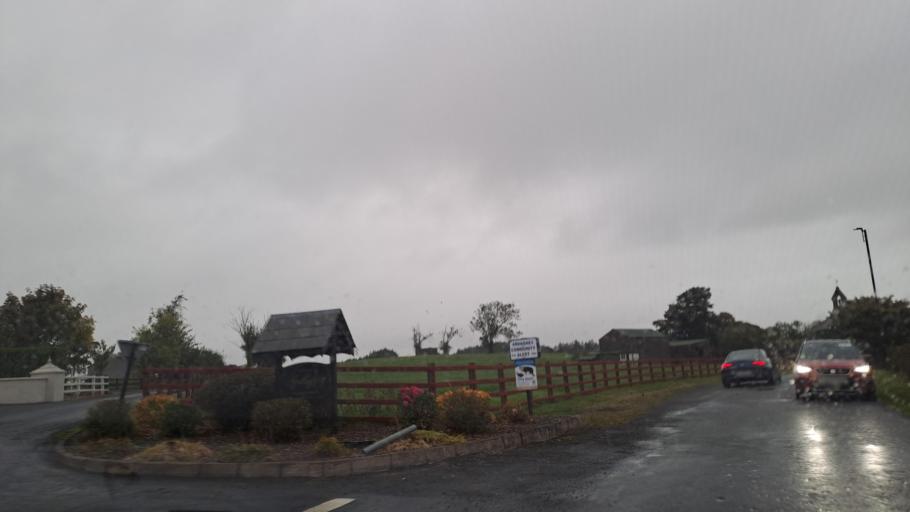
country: IE
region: Ulster
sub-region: County Monaghan
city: Monaghan
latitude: 54.2114
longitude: -6.9092
